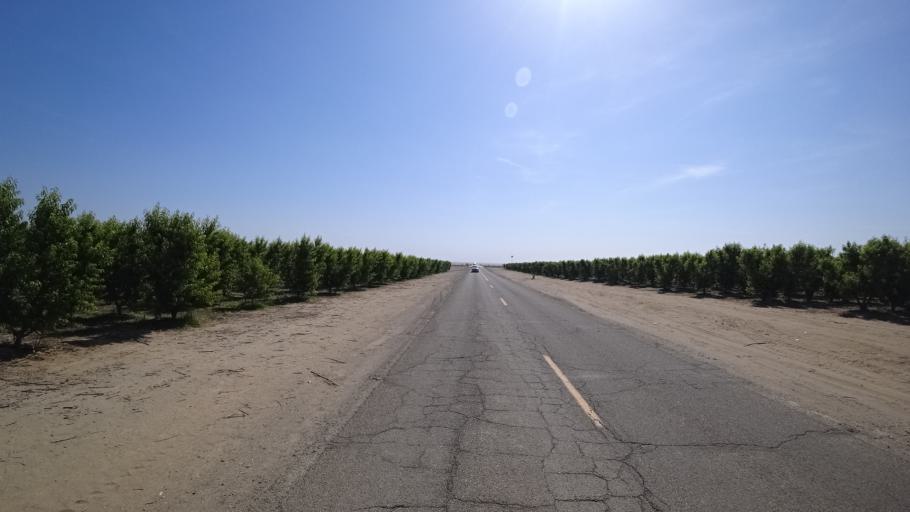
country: US
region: California
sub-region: Kings County
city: Kettleman City
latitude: 36.0363
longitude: -119.9960
